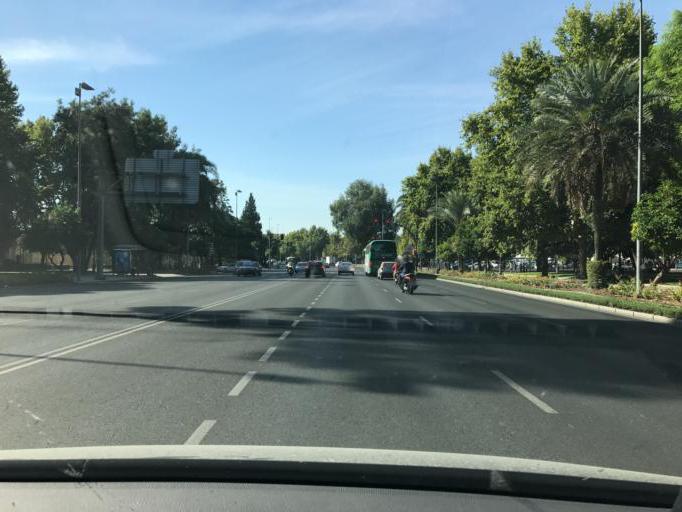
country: ES
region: Andalusia
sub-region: Province of Cordoba
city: Cordoba
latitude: 37.8766
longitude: -4.7863
